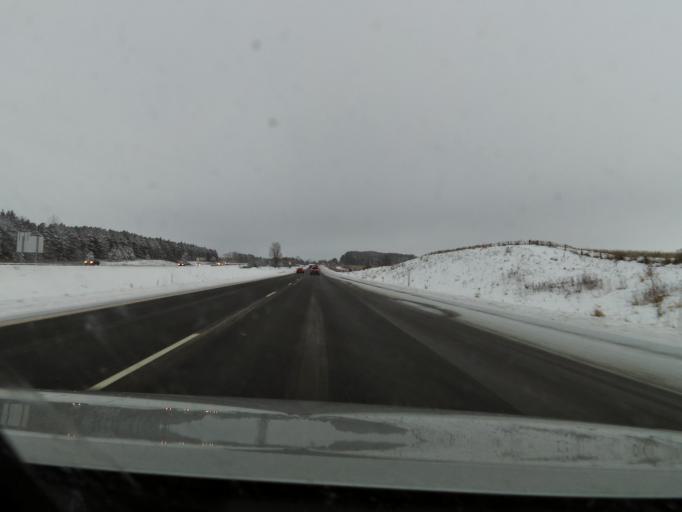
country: US
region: Wisconsin
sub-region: Saint Croix County
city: Baldwin
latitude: 44.9379
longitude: -92.3683
